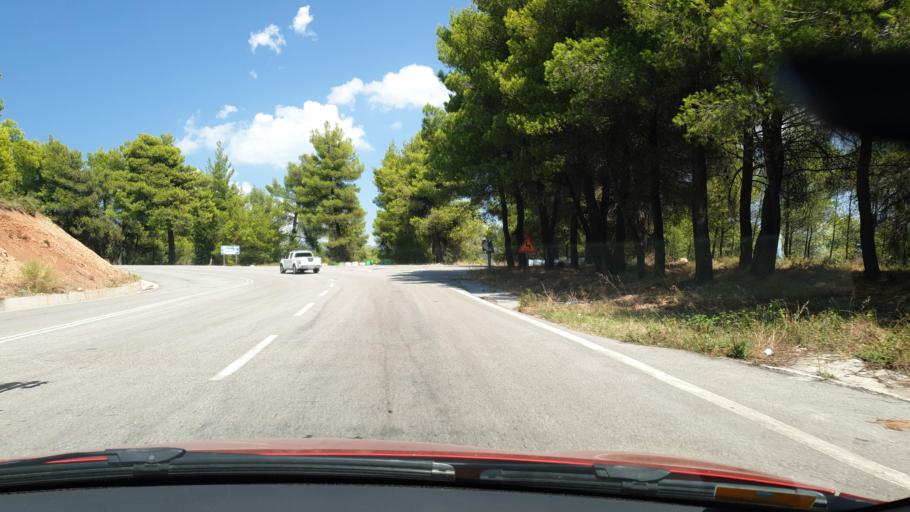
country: GR
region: Central Greece
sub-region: Nomos Evvoias
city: Politika
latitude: 38.6334
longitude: 23.5676
